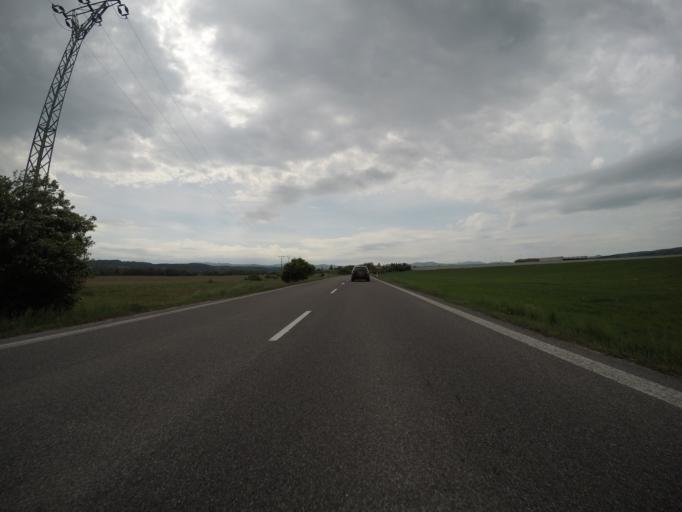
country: SK
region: Banskobystricky
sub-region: Okres Banska Bystrica
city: Zvolen
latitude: 48.6478
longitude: 19.1421
